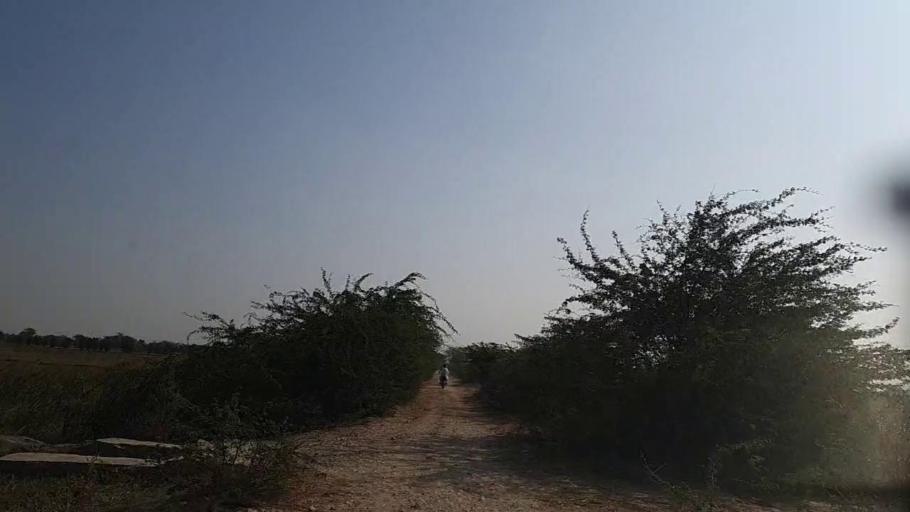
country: PK
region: Sindh
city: Mirpur Batoro
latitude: 24.6150
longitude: 68.2832
